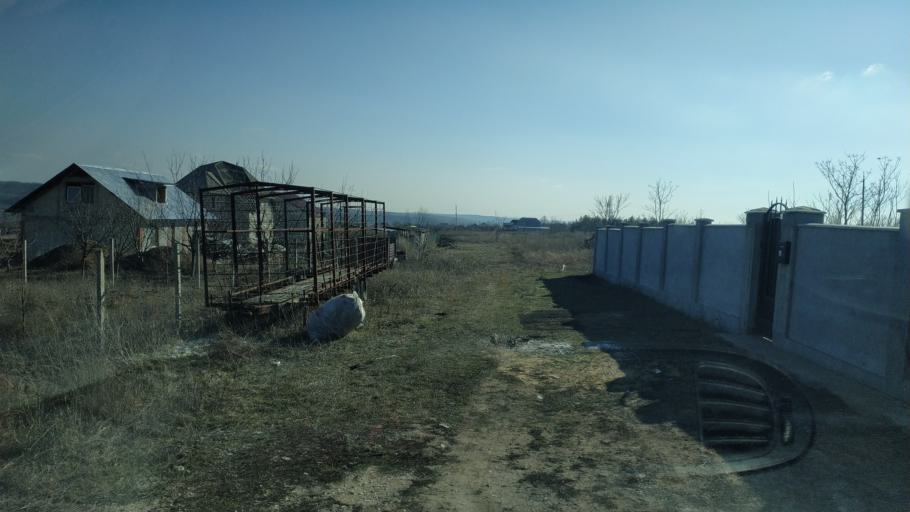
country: MD
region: Hincesti
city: Hincesti
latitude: 46.7524
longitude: 28.5180
